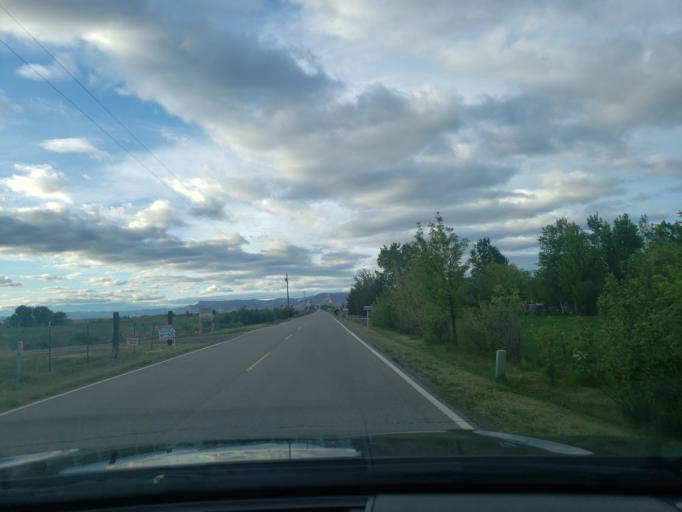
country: US
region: Colorado
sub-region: Mesa County
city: Fruita
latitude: 39.2177
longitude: -108.7197
